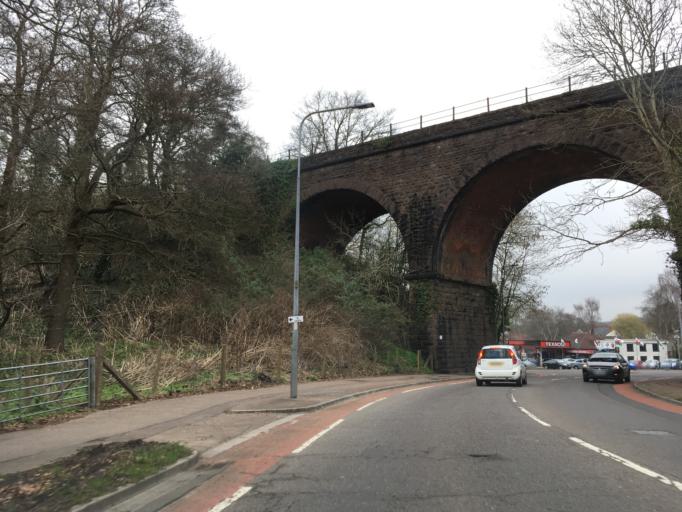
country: GB
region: Wales
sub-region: Cardiff
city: Cardiff
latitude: 51.5183
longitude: -3.1823
